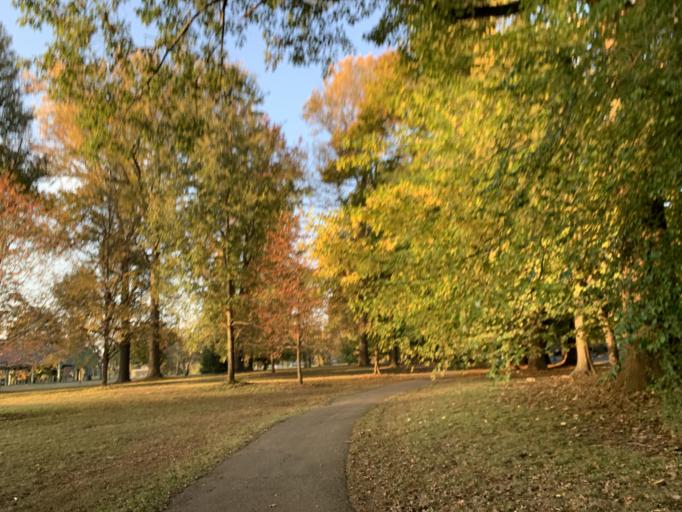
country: US
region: Kentucky
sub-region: Jefferson County
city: Shively
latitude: 38.2420
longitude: -85.8306
